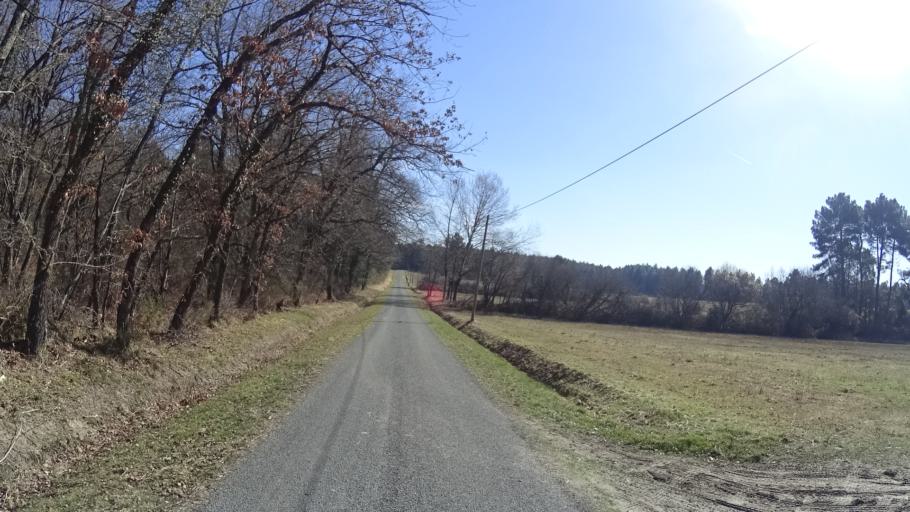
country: FR
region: Aquitaine
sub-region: Departement de la Dordogne
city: Saint-Aulaye
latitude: 45.1373
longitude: 0.2103
